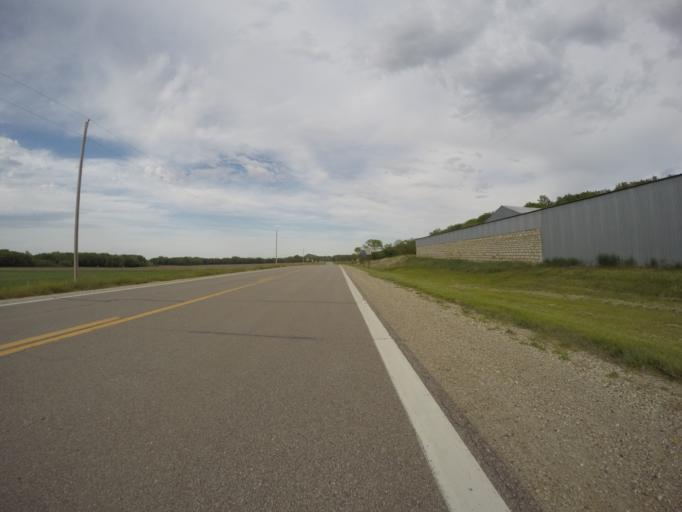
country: US
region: Kansas
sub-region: Riley County
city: Ogden
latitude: 39.1051
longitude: -96.6332
